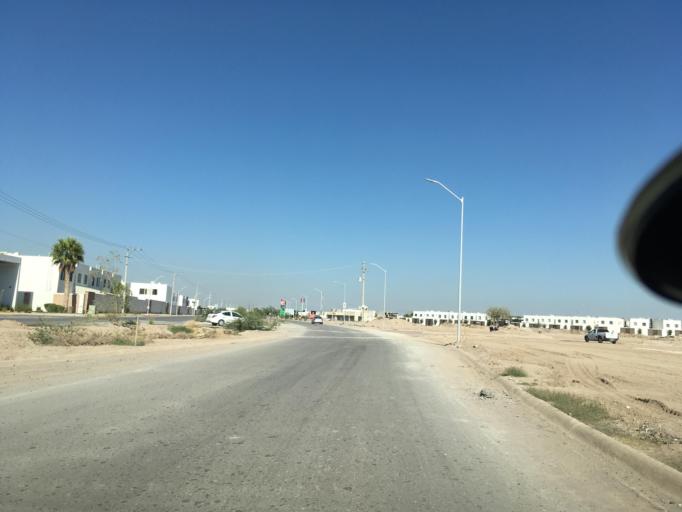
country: MX
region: Coahuila
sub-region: Torreon
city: Fraccionamiento la Noria
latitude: 25.5713
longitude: -103.3625
